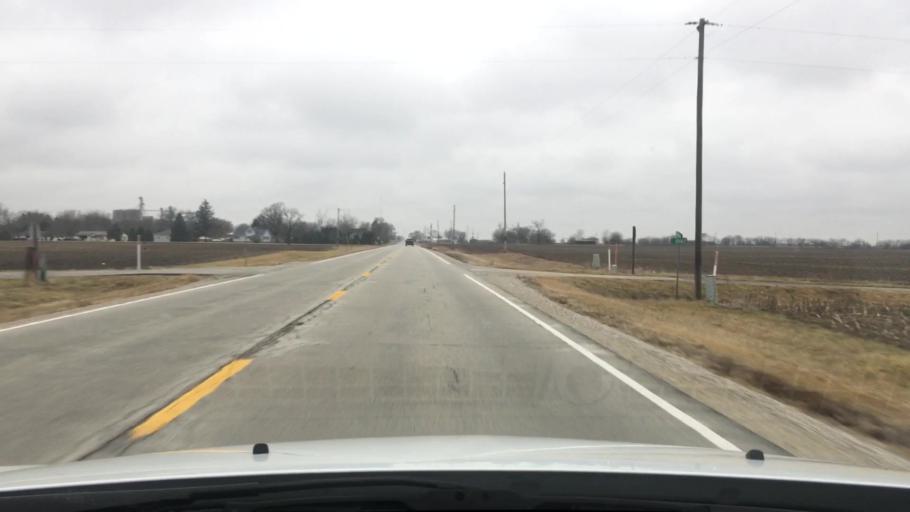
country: US
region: Illinois
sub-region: Iroquois County
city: Clifton
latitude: 40.8851
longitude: -87.9421
